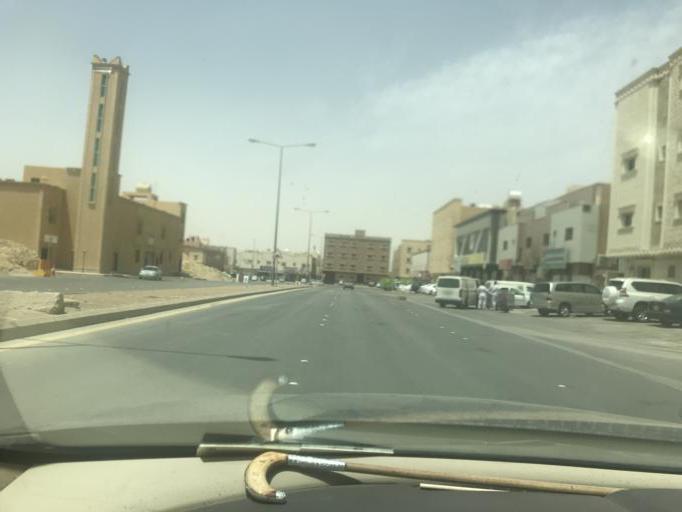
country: SA
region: Ar Riyad
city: Riyadh
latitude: 24.7982
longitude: 46.6665
